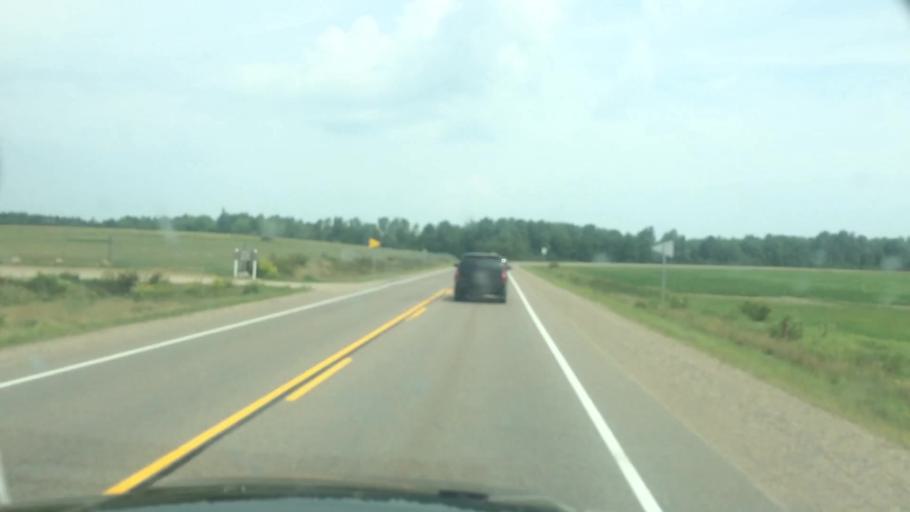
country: US
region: Wisconsin
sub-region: Langlade County
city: Antigo
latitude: 45.1592
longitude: -89.1618
